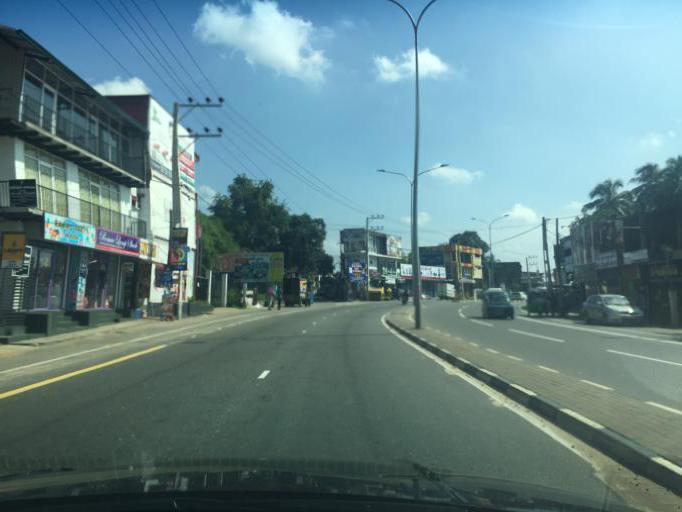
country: LK
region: Western
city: Maharagama
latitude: 6.8178
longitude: 79.9183
